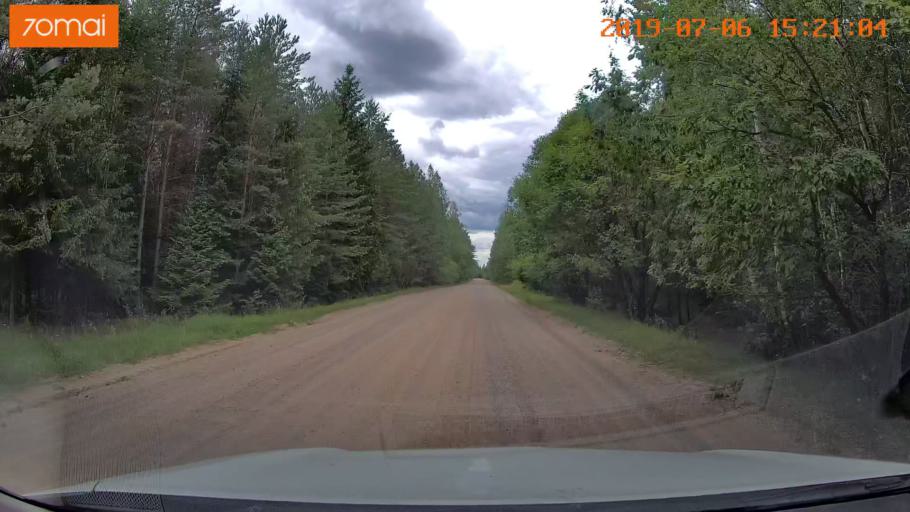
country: BY
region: Minsk
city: Valozhyn
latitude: 54.0093
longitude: 26.6219
